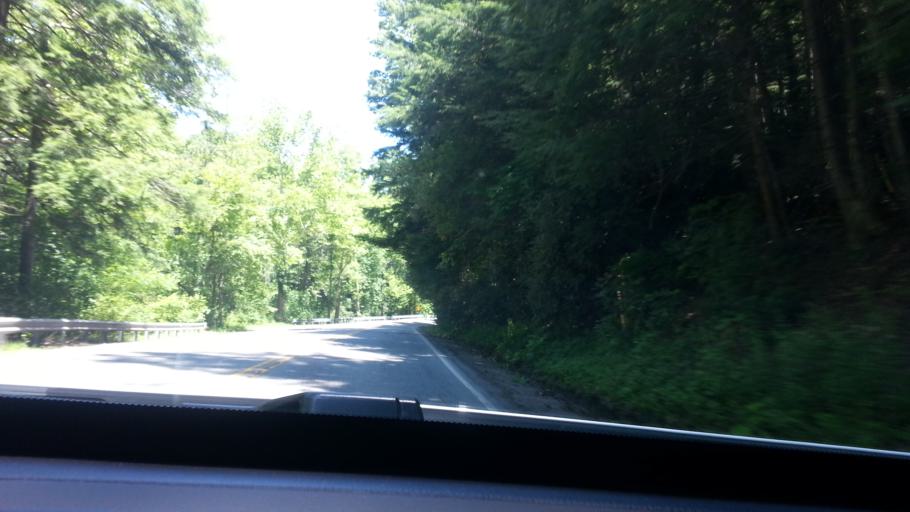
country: US
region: West Virginia
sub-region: Fayette County
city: Ansted
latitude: 38.0989
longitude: -81.1536
